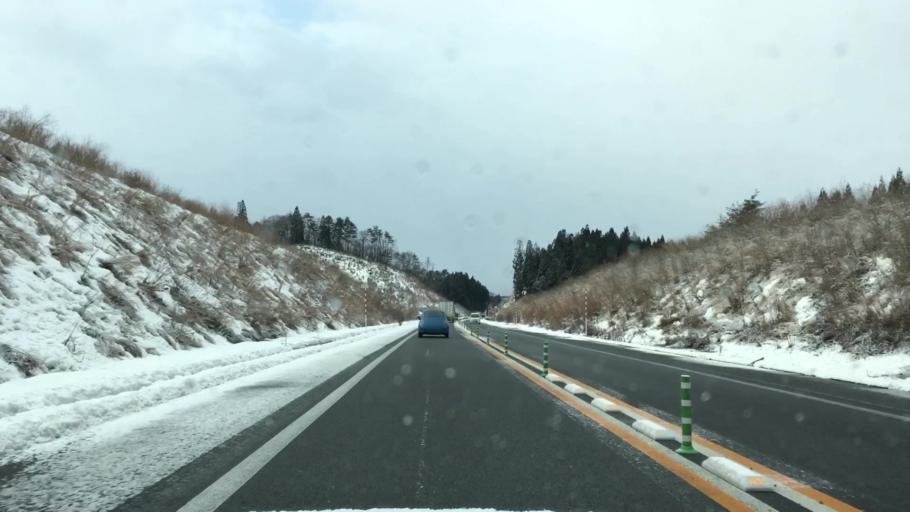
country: JP
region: Akita
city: Takanosu
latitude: 40.2116
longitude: 140.4165
